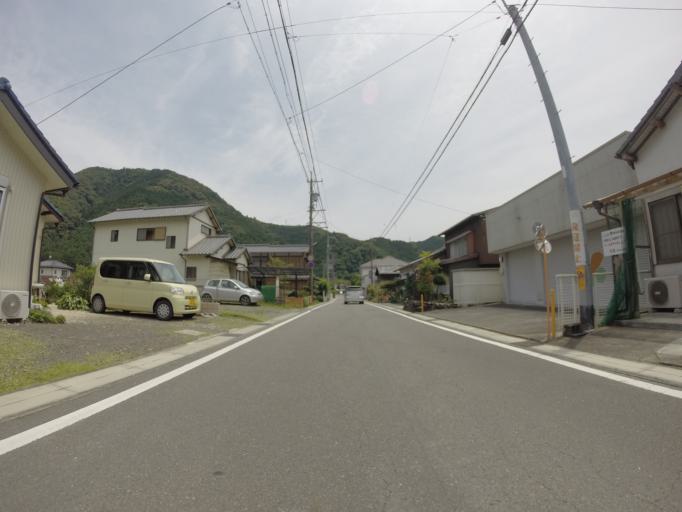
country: JP
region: Shizuoka
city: Shizuoka-shi
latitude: 35.0063
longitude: 138.2816
